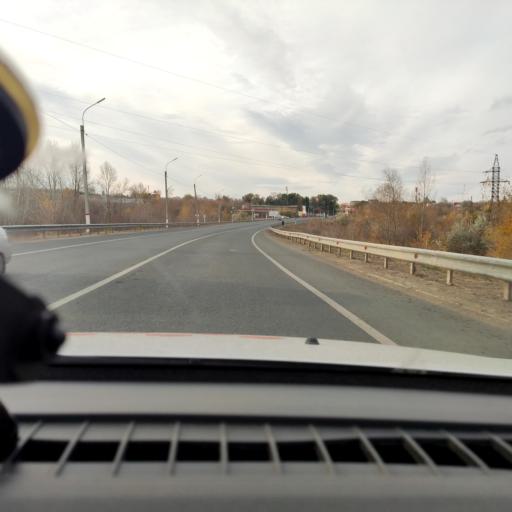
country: RU
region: Samara
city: Novokuybyshevsk
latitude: 53.1232
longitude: 49.9446
